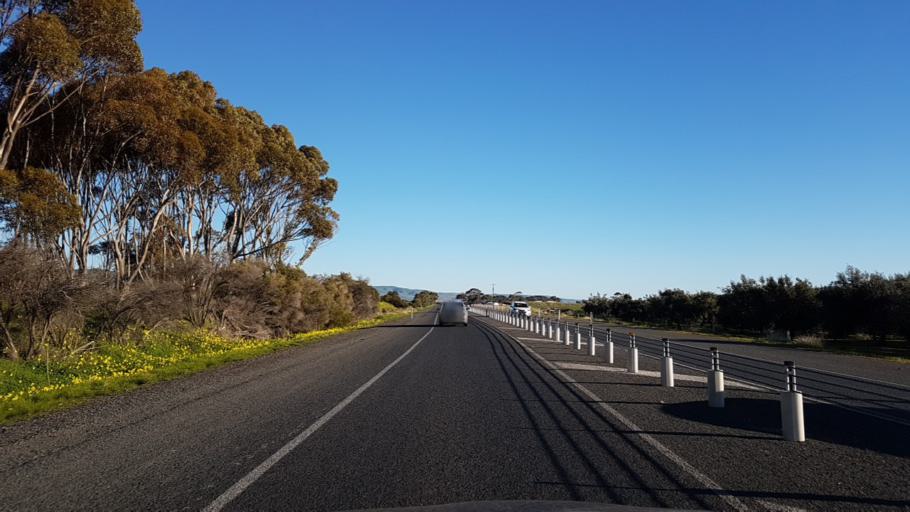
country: AU
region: South Australia
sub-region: Onkaparinga
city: Aldinga
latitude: -35.2553
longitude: 138.4938
